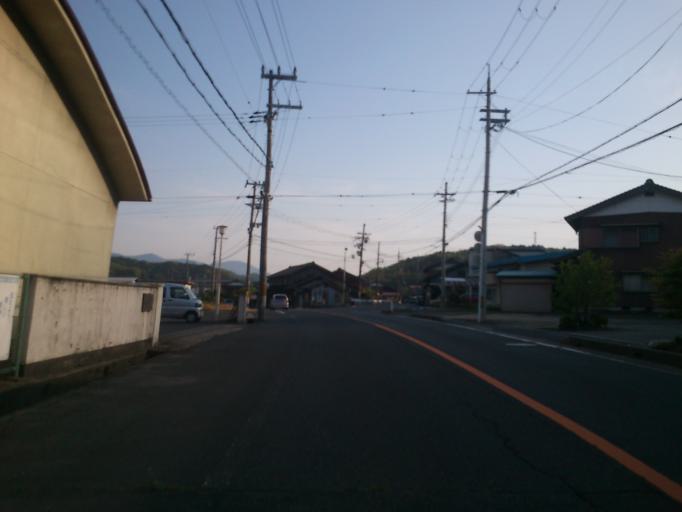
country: JP
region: Kyoto
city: Miyazu
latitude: 35.5571
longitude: 135.1395
